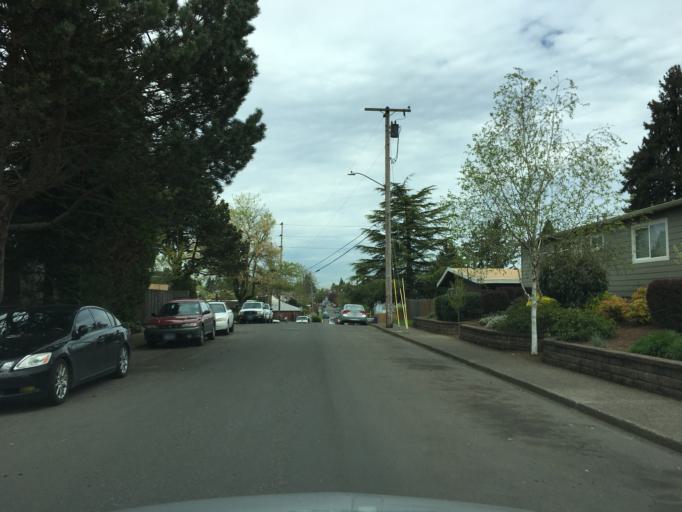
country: US
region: Oregon
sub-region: Multnomah County
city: Lents
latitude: 45.5218
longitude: -122.5880
